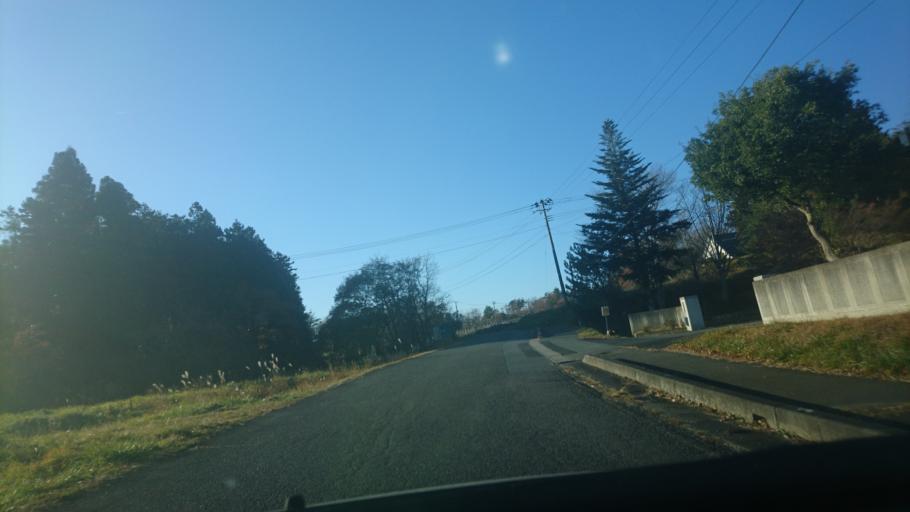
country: JP
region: Iwate
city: Ichinoseki
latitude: 38.8962
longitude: 141.2364
